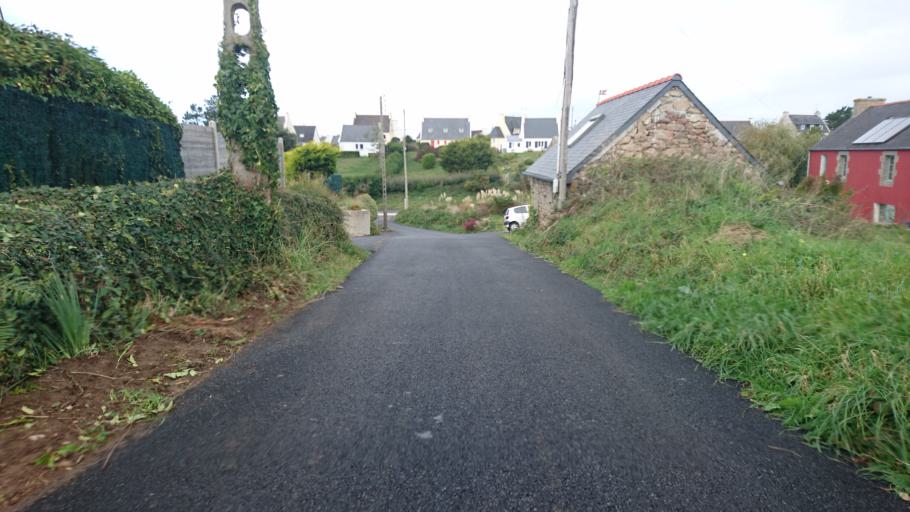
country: FR
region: Brittany
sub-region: Departement du Finistere
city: Lampaul-Plouarzel
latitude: 48.4446
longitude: -4.7683
